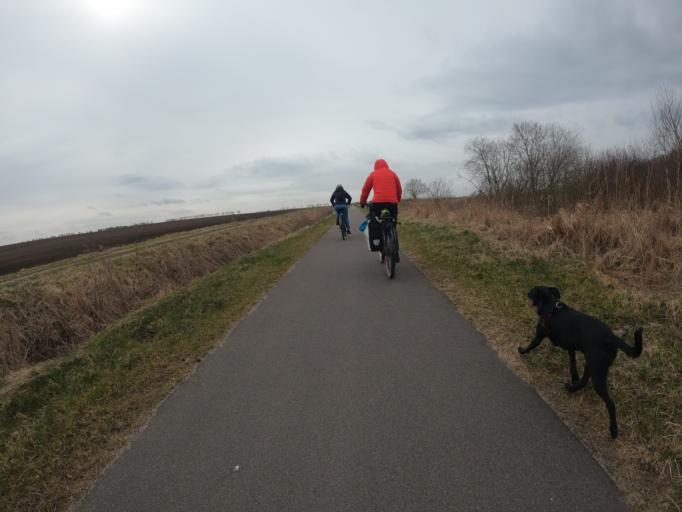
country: PL
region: West Pomeranian Voivodeship
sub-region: Powiat gryficki
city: Mrzezyno
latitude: 54.1101
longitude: 15.2955
